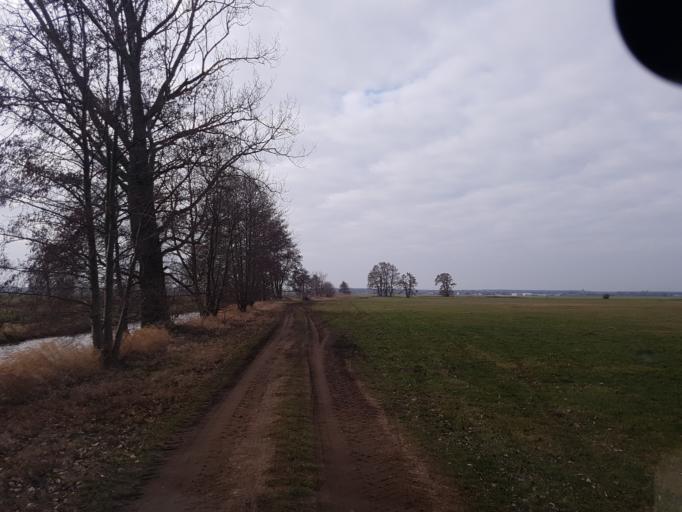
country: DE
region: Brandenburg
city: Schonewalde
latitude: 51.6658
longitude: 13.5692
